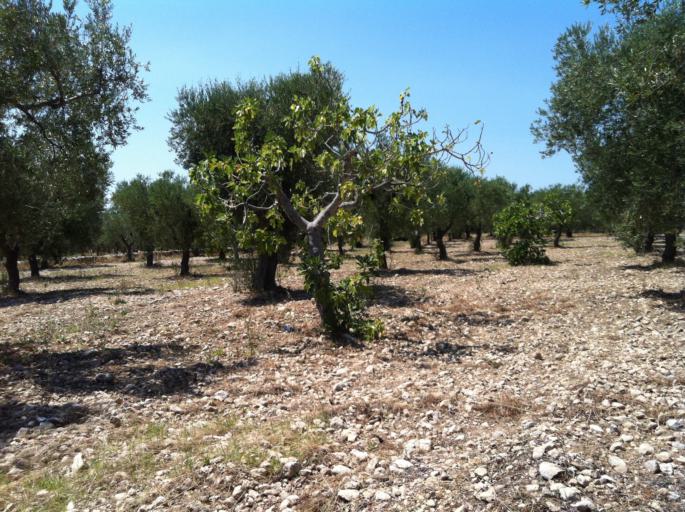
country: IT
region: Apulia
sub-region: Provincia di Foggia
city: Monte Sant'Angelo
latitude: 41.6626
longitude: 15.9528
